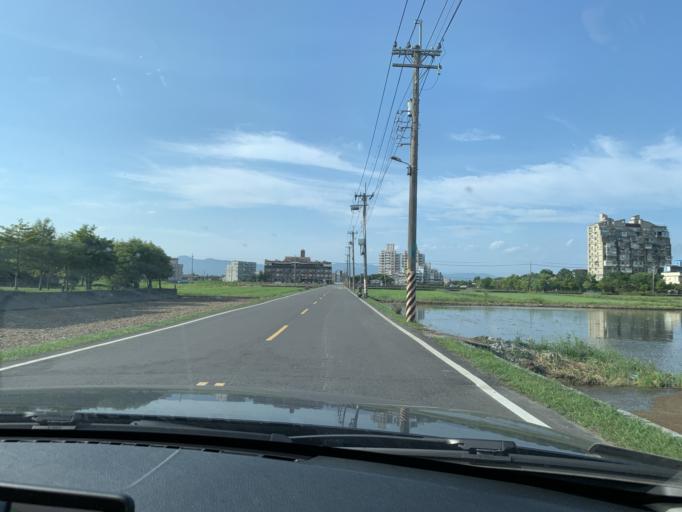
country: TW
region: Taiwan
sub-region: Yilan
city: Yilan
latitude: 24.6752
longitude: 121.8101
